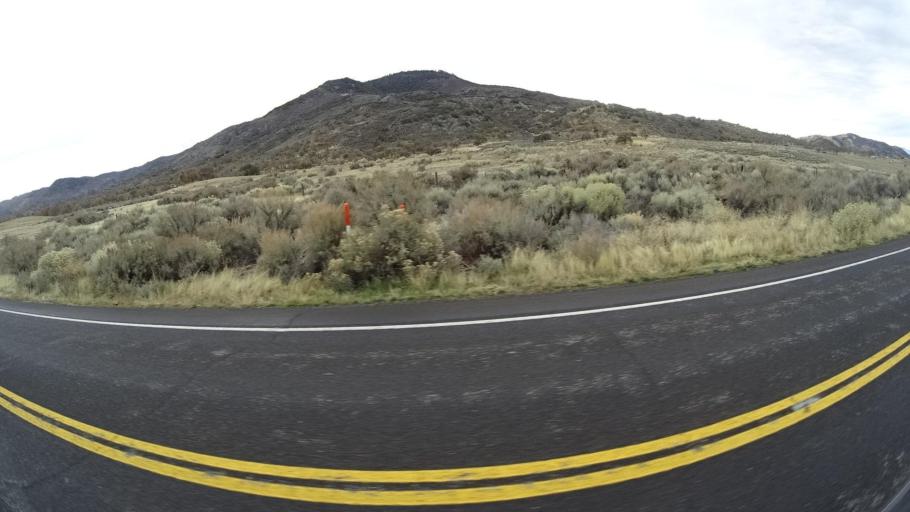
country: US
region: California
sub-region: Kern County
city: Stallion Springs
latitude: 35.0950
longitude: -118.5888
